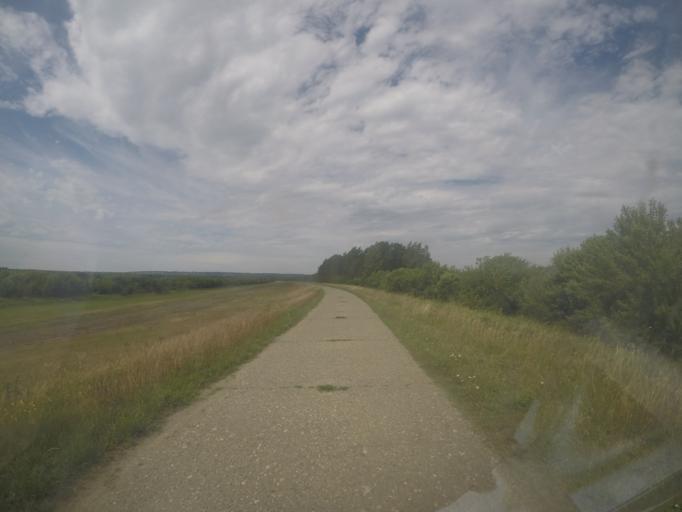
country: RS
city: Knicanin
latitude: 45.1778
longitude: 20.3004
